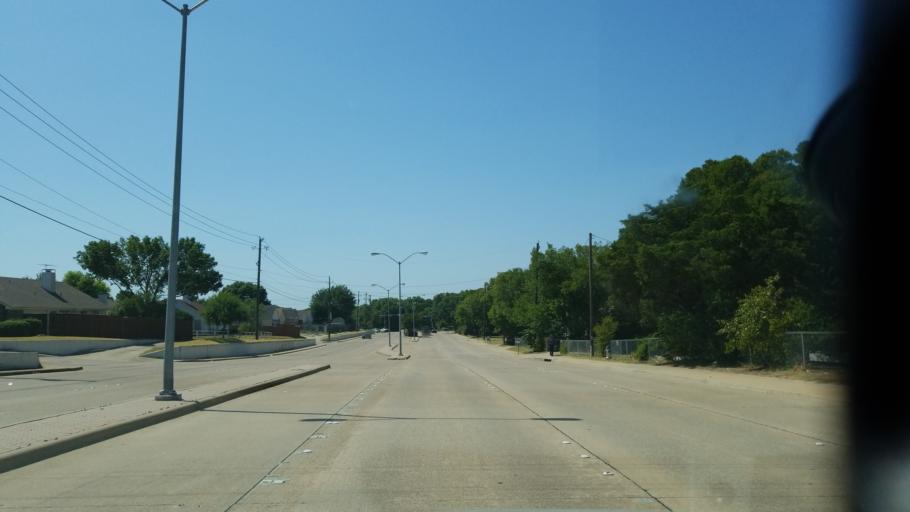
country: US
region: Texas
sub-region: Dallas County
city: Duncanville
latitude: 32.6355
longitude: -96.8913
